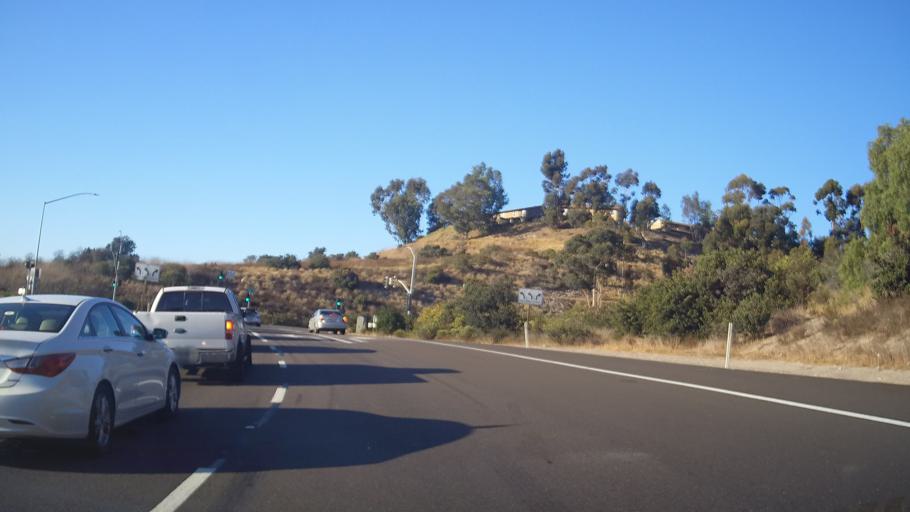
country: US
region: California
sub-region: San Diego County
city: La Mesa
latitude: 32.8099
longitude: -117.1125
